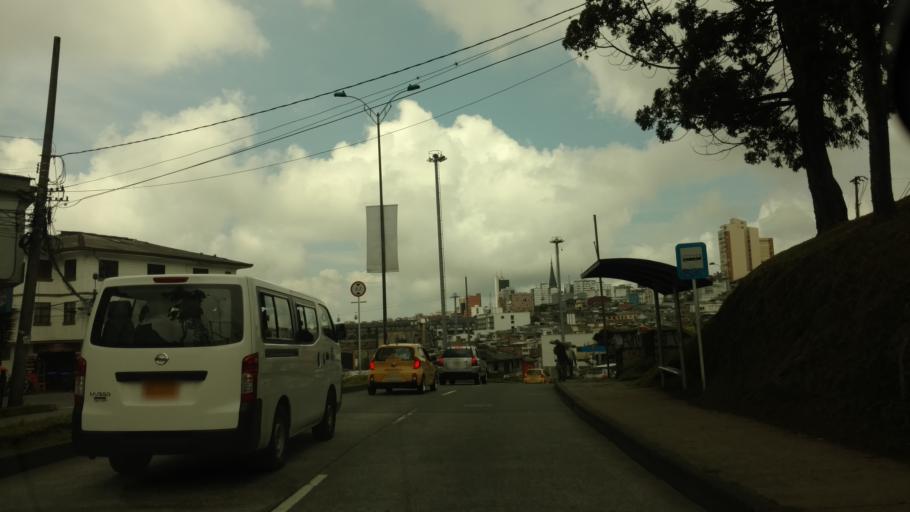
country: CO
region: Caldas
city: Manizales
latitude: 5.0654
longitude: -75.5068
